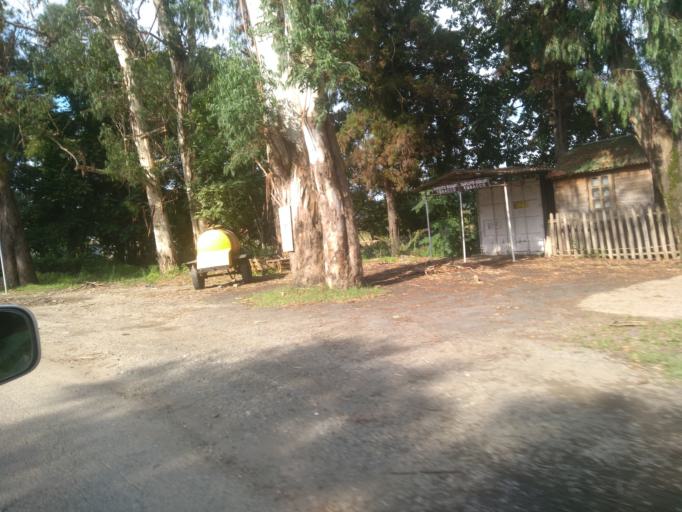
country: GE
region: Ajaria
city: Khelvachauri
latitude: 41.5863
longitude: 41.6508
